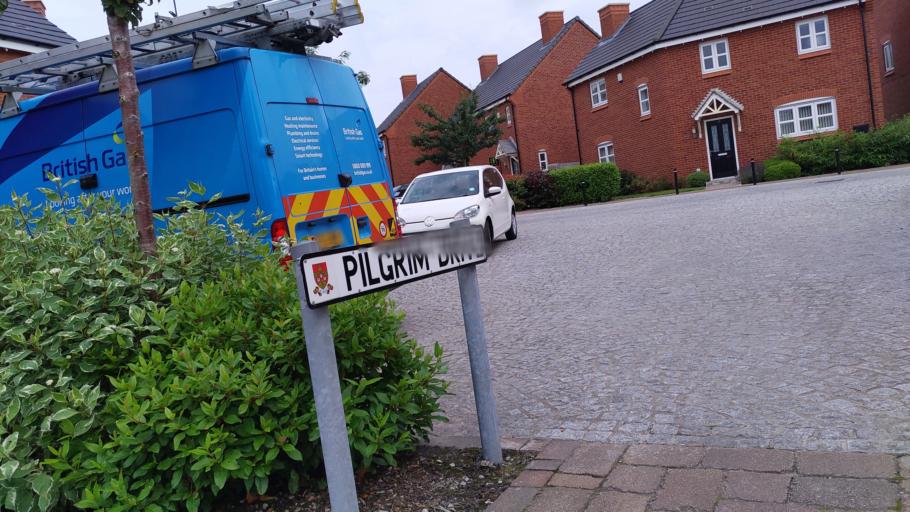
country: GB
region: England
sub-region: Lancashire
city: Coppull
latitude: 53.6300
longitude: -2.6365
